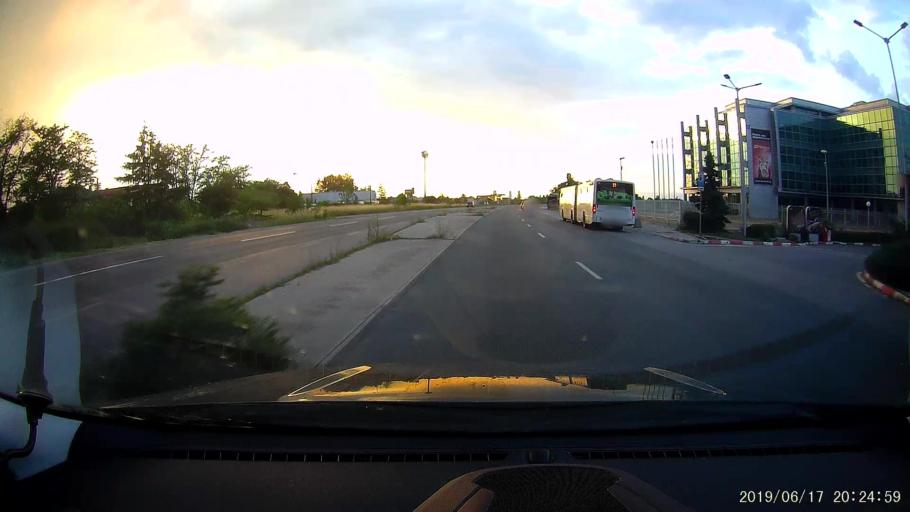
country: BG
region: Sofiya
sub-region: Obshtina Bozhurishte
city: Bozhurishte
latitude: 42.7456
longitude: 23.2290
